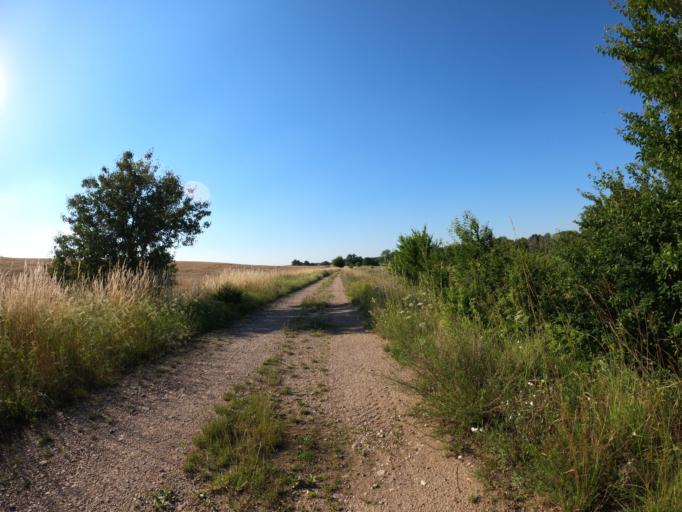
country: DE
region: Brandenburg
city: Gartz
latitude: 53.2254
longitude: 14.3699
